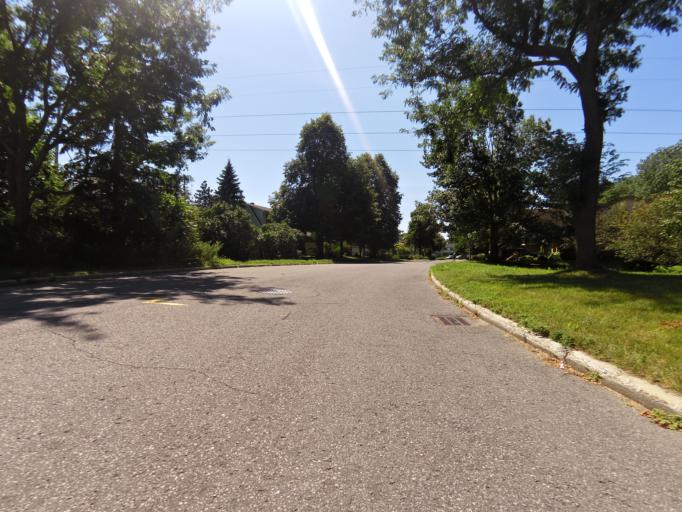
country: CA
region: Ontario
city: Ottawa
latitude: 45.3462
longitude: -75.6710
